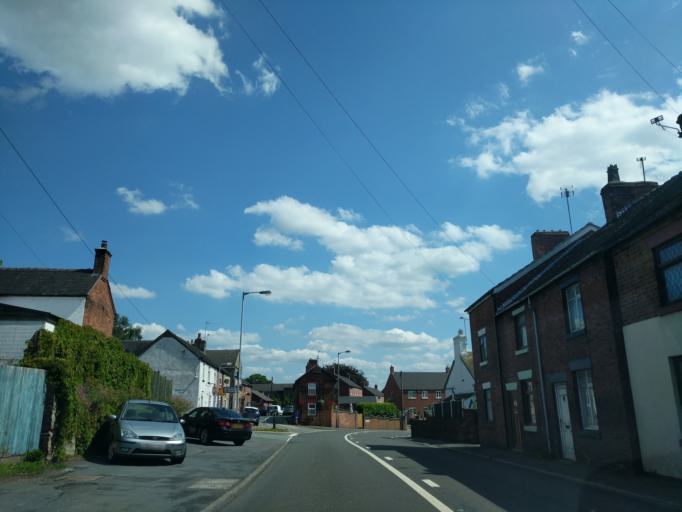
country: GB
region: England
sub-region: Staffordshire
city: Cheadle
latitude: 52.9555
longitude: -1.9877
